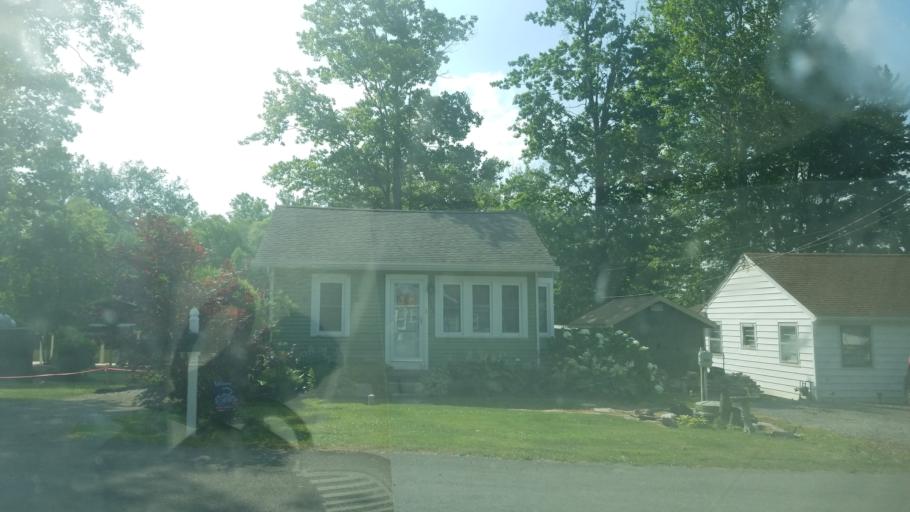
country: US
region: Ohio
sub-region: Logan County
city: Russells Point
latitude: 40.5025
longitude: -83.8560
